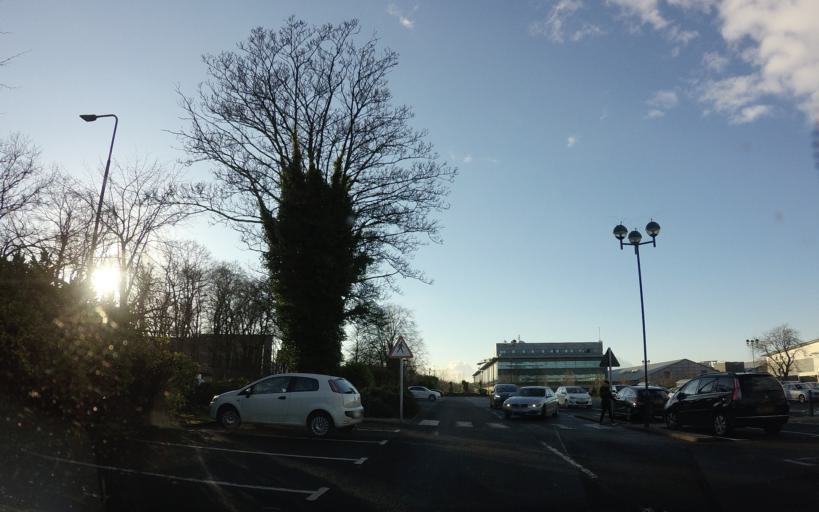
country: GB
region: Scotland
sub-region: Edinburgh
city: Edinburgh
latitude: 55.9692
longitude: -3.2309
